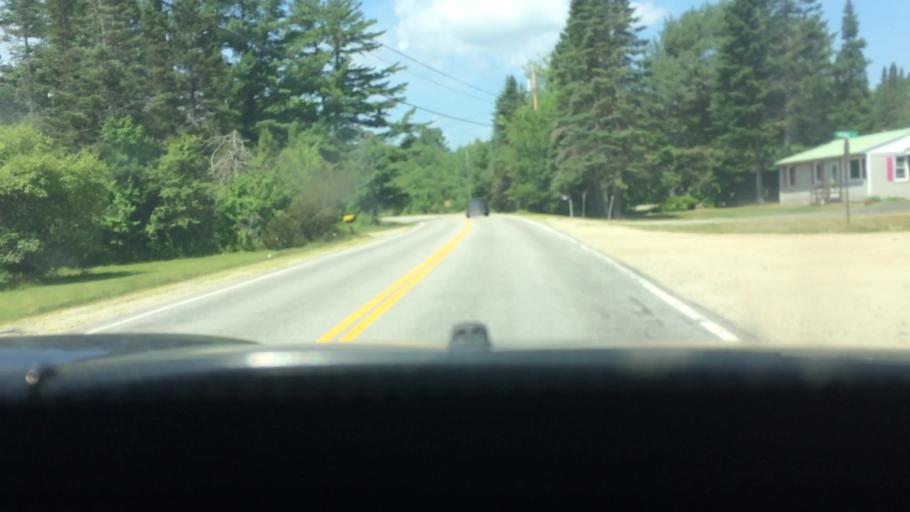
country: US
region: Maine
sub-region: Oxford County
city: Oxford
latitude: 44.1342
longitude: -70.4532
